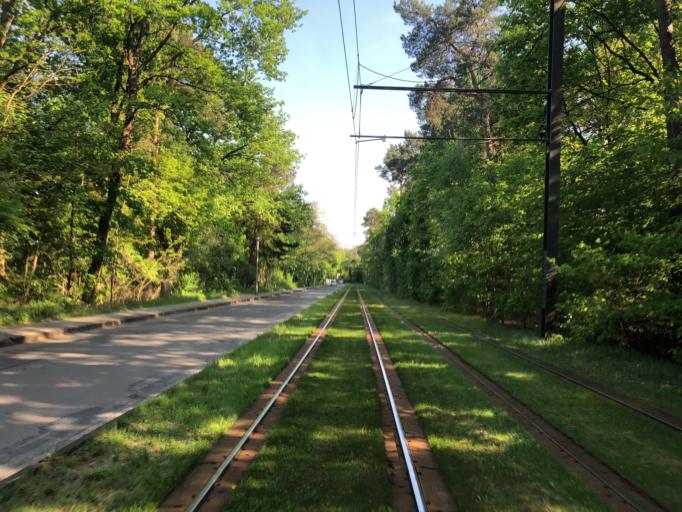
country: DE
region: Berlin
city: Schmockwitz
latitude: 52.3990
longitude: 13.6265
